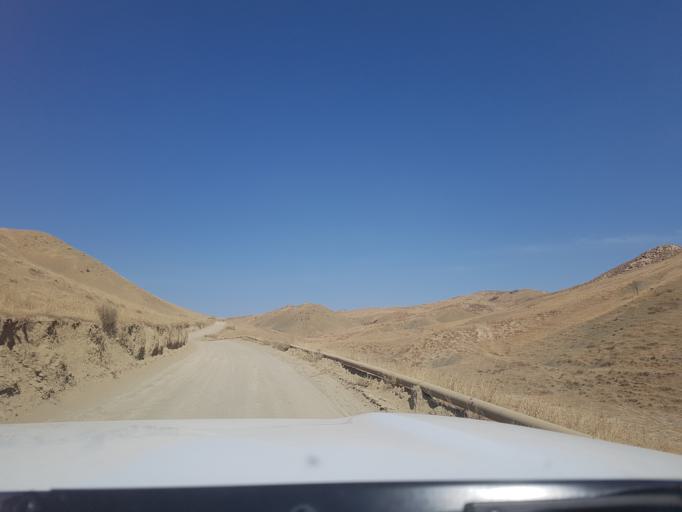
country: TM
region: Ahal
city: Baharly
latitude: 38.2580
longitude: 56.8887
